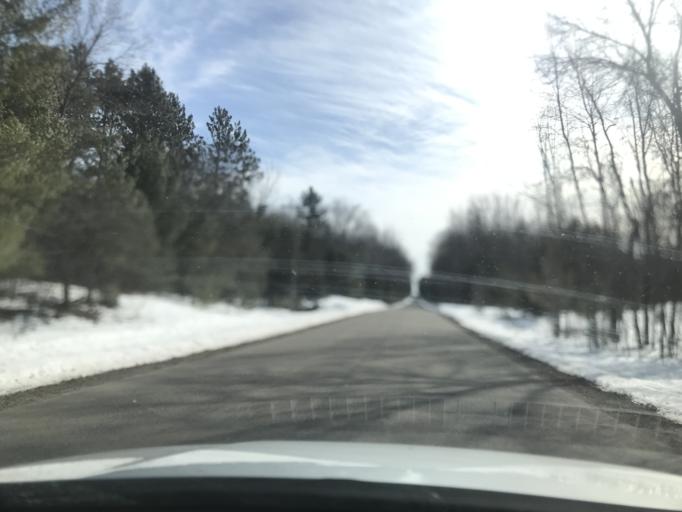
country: US
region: Wisconsin
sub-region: Marinette County
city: Peshtigo
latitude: 45.2151
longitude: -87.7794
